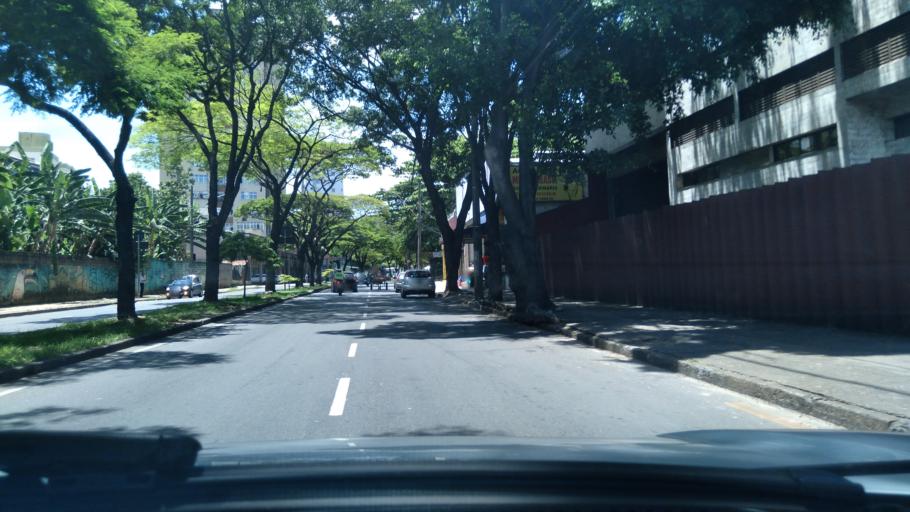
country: BR
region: Minas Gerais
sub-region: Contagem
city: Contagem
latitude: -19.9275
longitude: -43.9960
